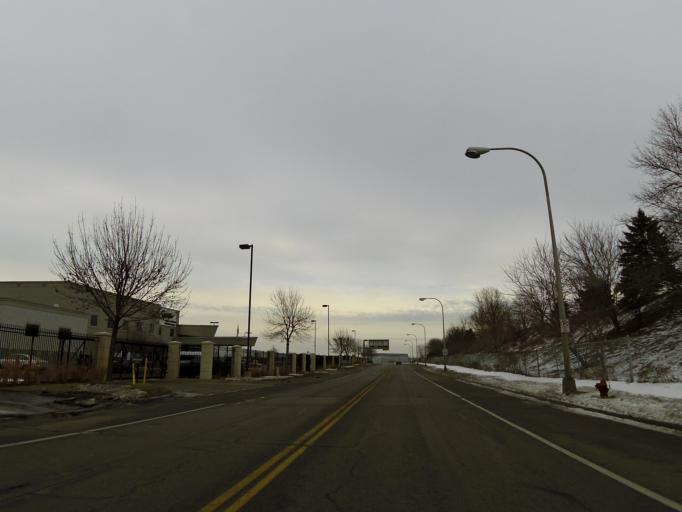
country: US
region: Minnesota
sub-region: Hennepin County
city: Richfield
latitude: 44.8765
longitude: -93.2185
